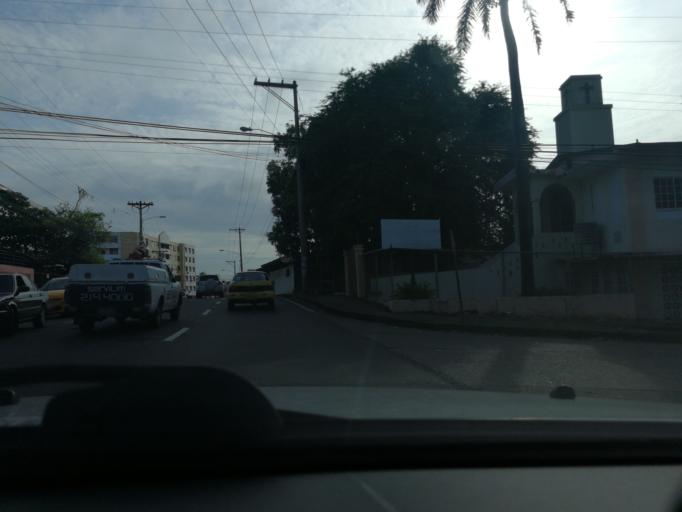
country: PA
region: Panama
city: Panama
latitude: 9.0172
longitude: -79.5034
